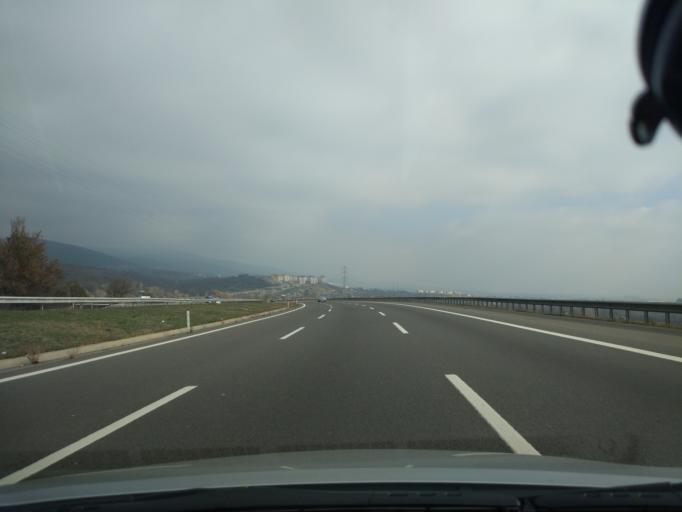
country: TR
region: Bolu
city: Bolu
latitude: 40.7331
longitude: 31.5298
